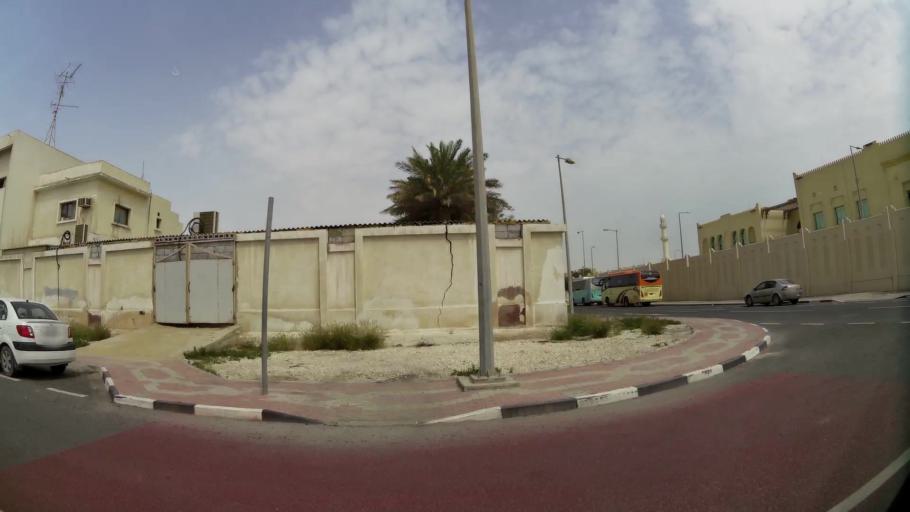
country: QA
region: Baladiyat ar Rayyan
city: Ar Rayyan
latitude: 25.3128
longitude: 51.4740
